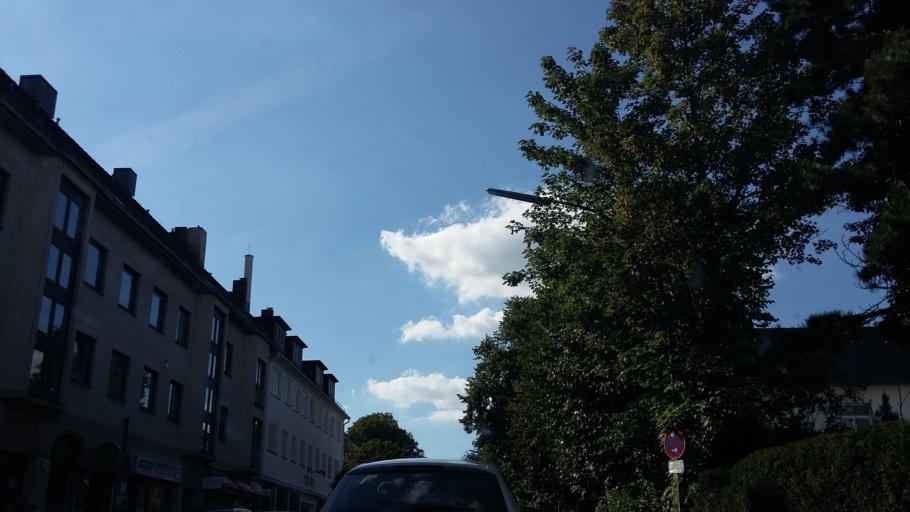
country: DE
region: Schleswig-Holstein
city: Halstenbek
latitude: 53.5625
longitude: 9.8174
